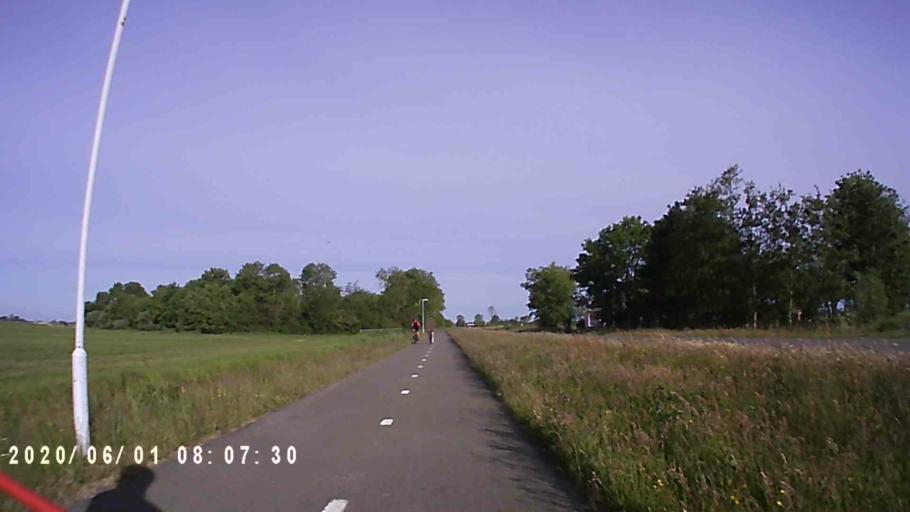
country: NL
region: Friesland
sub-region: Gemeente Ferwerderadiel
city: Burdaard
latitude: 53.2826
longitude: 5.9036
